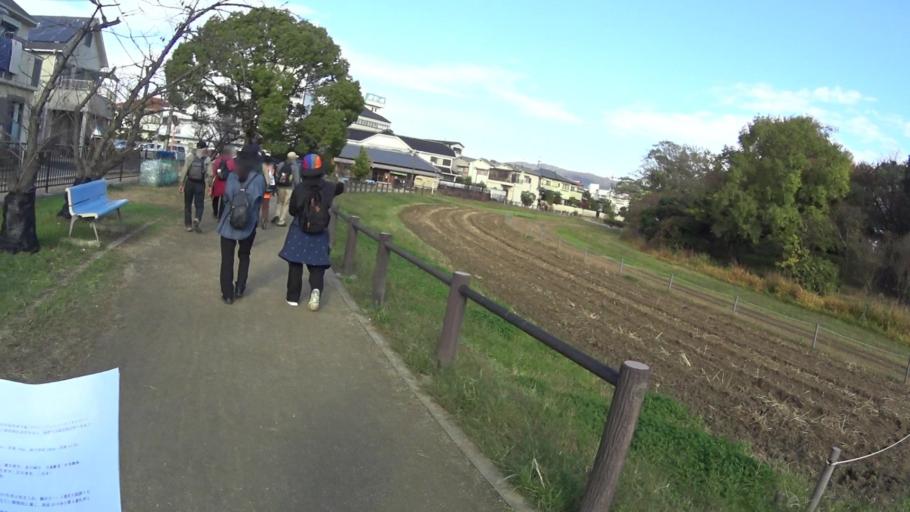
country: JP
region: Osaka
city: Kashihara
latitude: 34.5823
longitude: 135.5926
